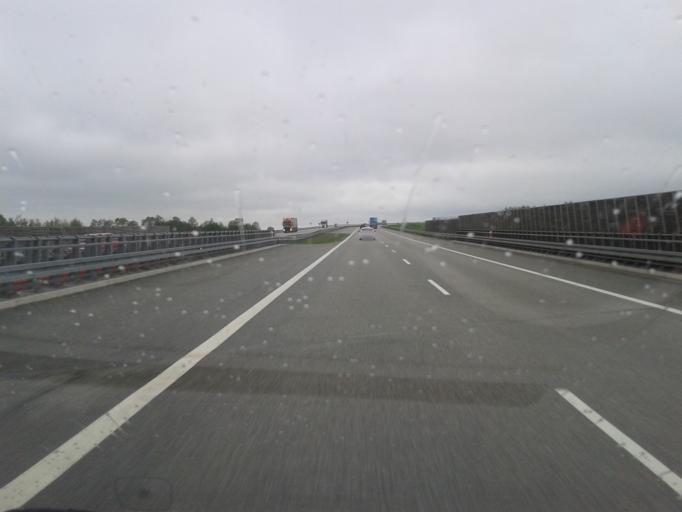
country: PL
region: Subcarpathian Voivodeship
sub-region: Powiat debicki
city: Zyrakow
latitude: 50.0887
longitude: 21.3255
